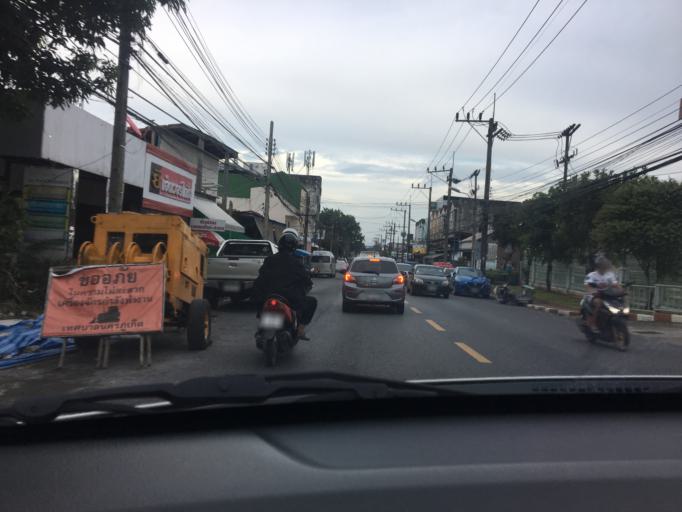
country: TH
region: Phuket
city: Phuket
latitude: 7.8878
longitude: 98.3984
